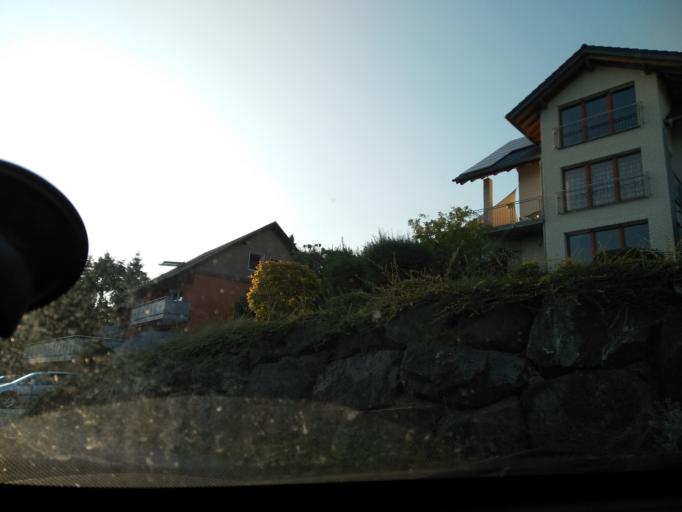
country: DE
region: Hesse
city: Dillenburg
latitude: 50.8161
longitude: 8.3476
